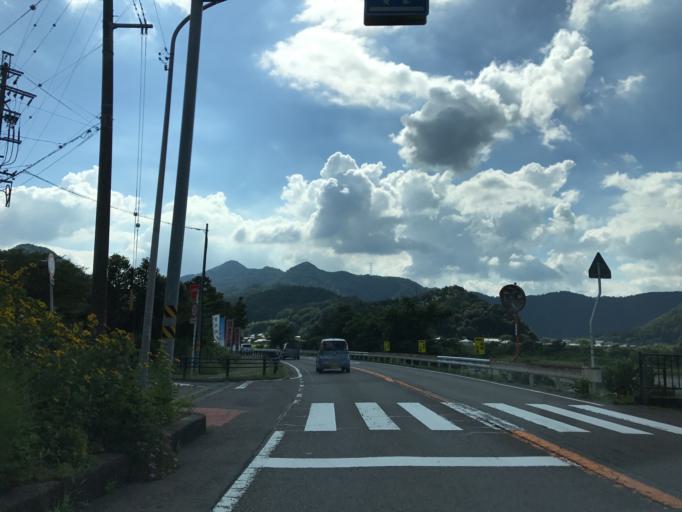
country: JP
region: Gifu
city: Mino
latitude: 35.5688
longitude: 136.9208
